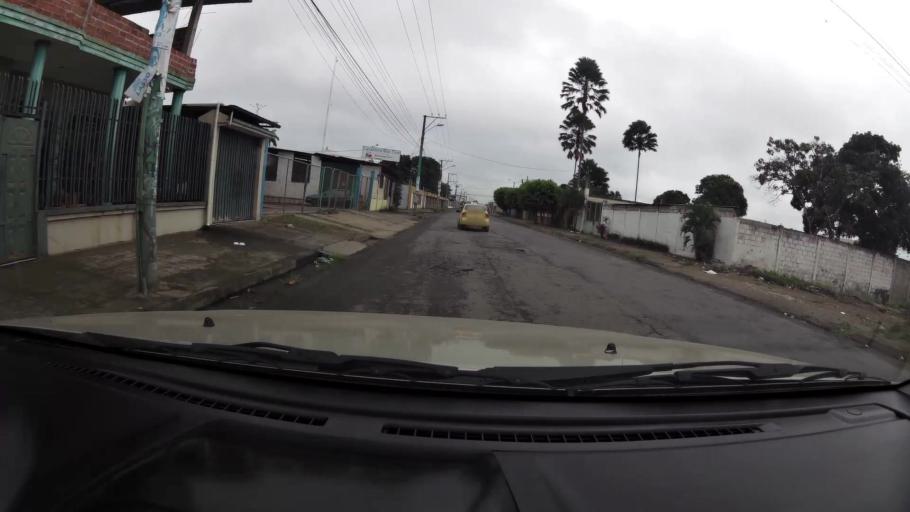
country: EC
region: El Oro
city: Pasaje
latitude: -3.3271
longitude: -79.8182
